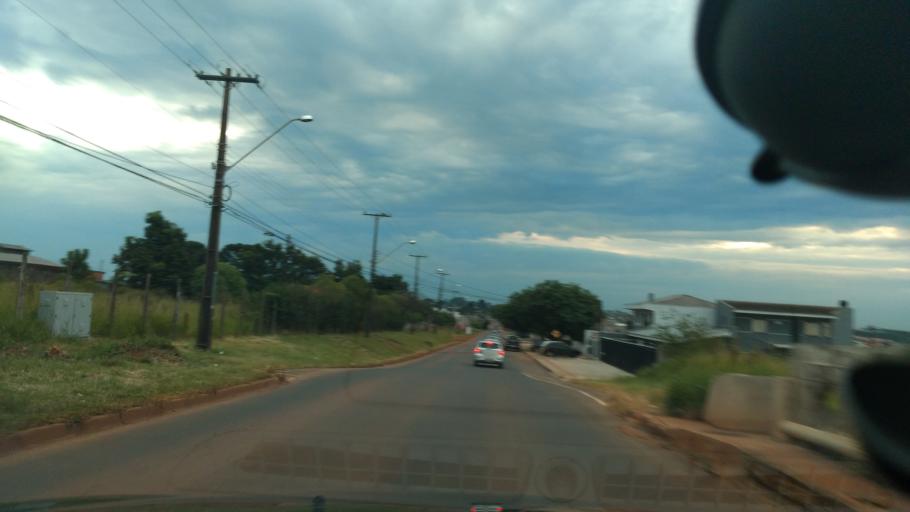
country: BR
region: Parana
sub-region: Guarapuava
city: Guarapuava
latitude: -25.3924
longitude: -51.4872
